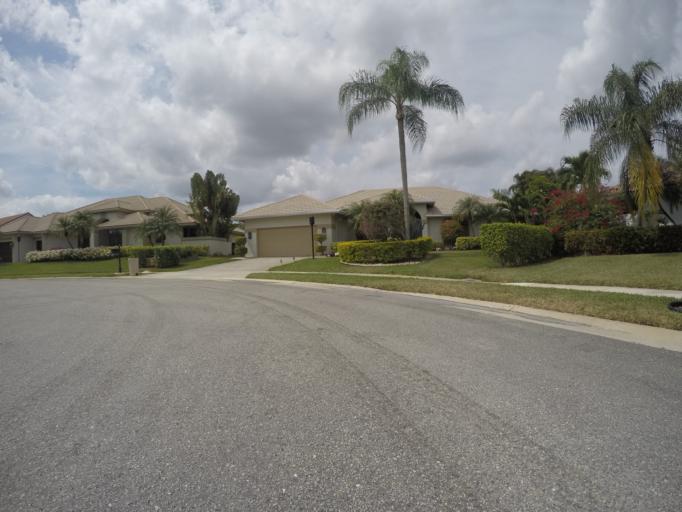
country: US
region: Florida
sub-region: Palm Beach County
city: Villages of Oriole
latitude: 26.4138
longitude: -80.2195
